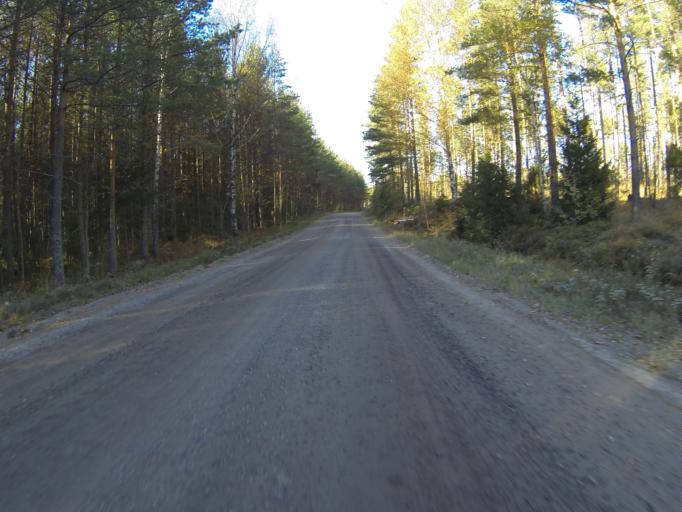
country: FI
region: Varsinais-Suomi
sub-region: Salo
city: Saerkisalo
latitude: 60.2256
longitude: 22.9835
